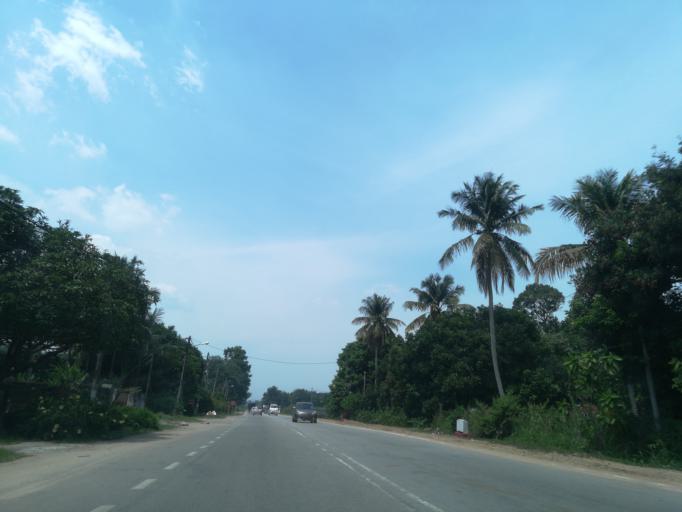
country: MY
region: Penang
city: Tasek Glugor
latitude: 5.4410
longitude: 100.5521
